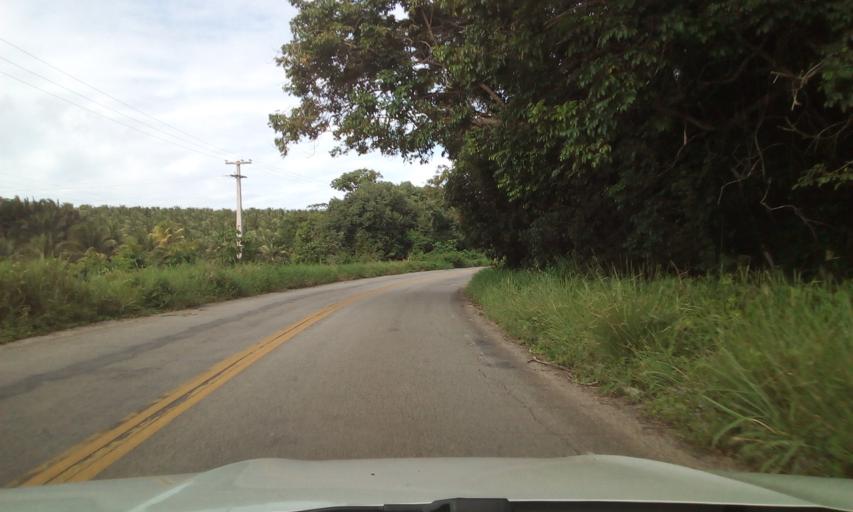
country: BR
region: Paraiba
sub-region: Cabedelo
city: Cabedelo
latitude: -6.9442
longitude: -34.9171
